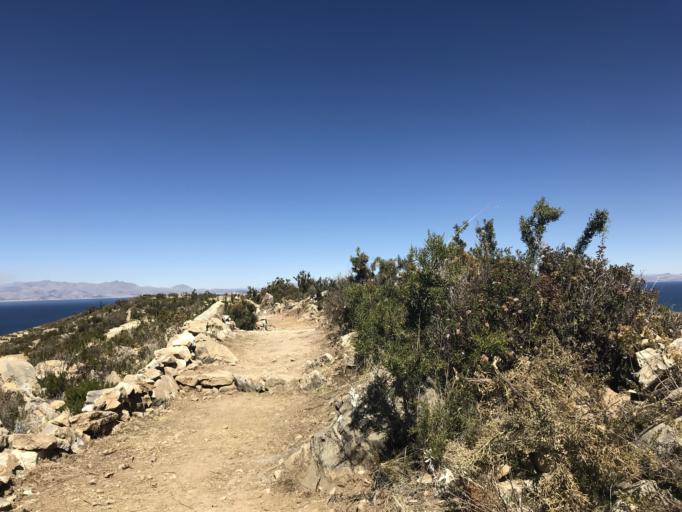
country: BO
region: La Paz
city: Yumani
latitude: -16.0449
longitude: -69.1461
